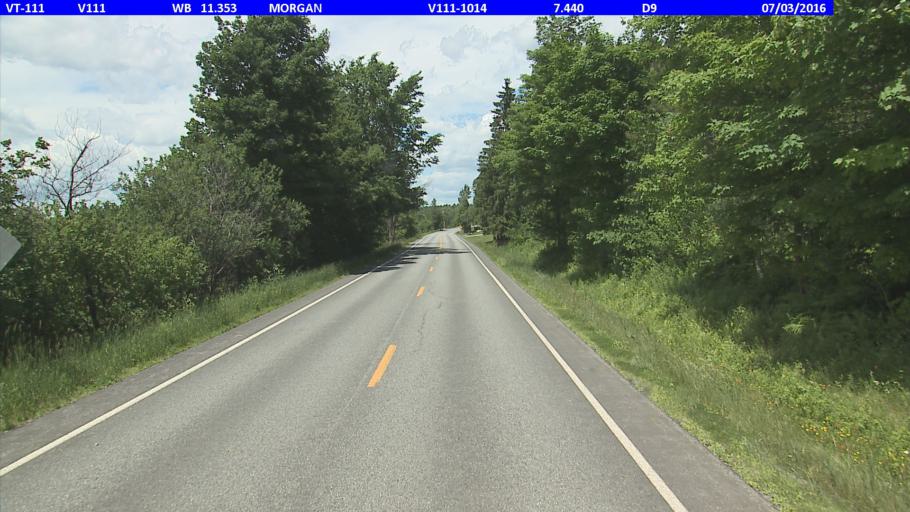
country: US
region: Vermont
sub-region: Orleans County
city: Newport
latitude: 44.8767
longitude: -71.9599
